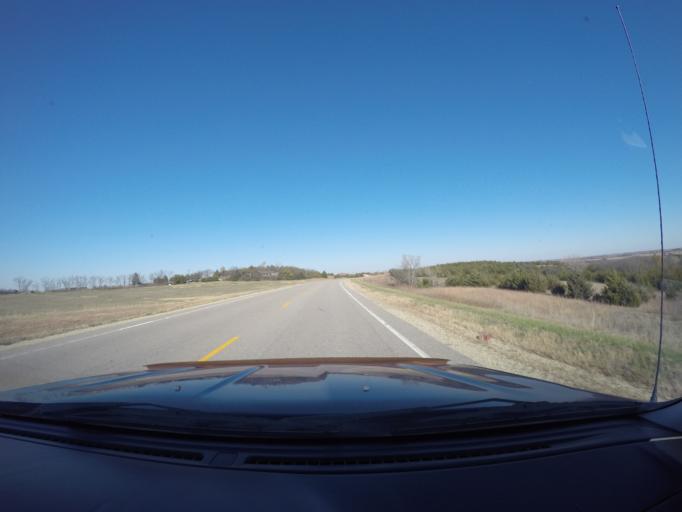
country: US
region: Kansas
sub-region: Riley County
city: Manhattan
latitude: 39.4013
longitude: -96.7629
